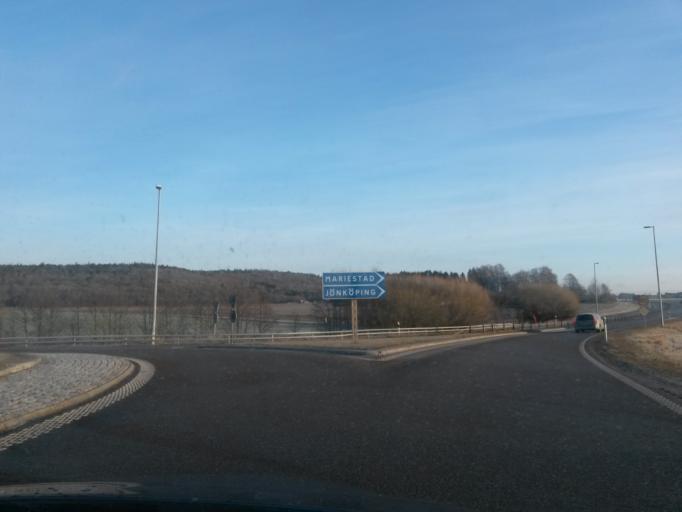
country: SE
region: Vaestra Goetaland
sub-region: Vanersborgs Kommun
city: Vargon
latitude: 58.2902
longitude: 12.3945
